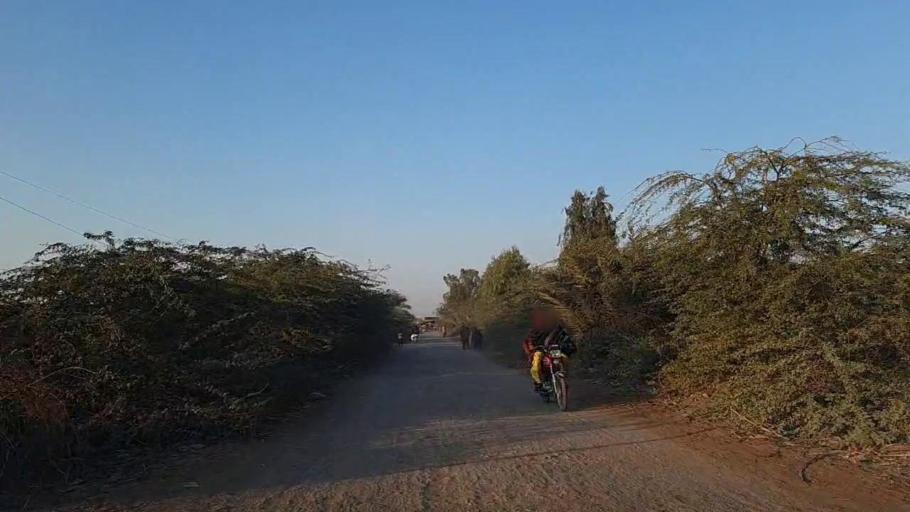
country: PK
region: Sindh
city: Nawabshah
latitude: 26.2529
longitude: 68.3411
